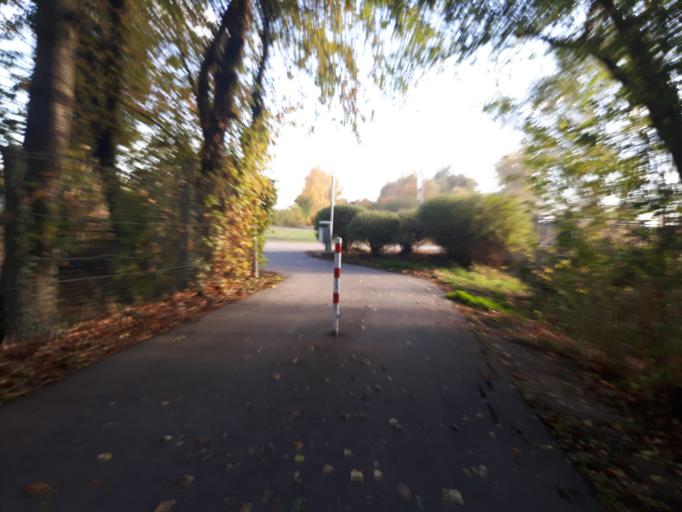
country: DE
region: Baden-Wuerttemberg
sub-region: Karlsruhe Region
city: Sankt Leon-Rot
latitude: 49.2612
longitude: 8.6198
